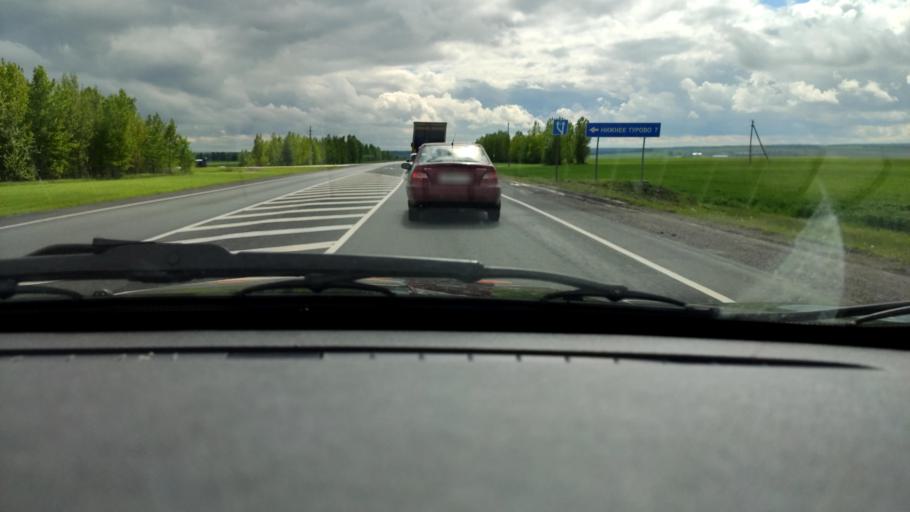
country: RU
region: Voronezj
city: Nizhnedevitsk
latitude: 51.6031
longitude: 38.6047
